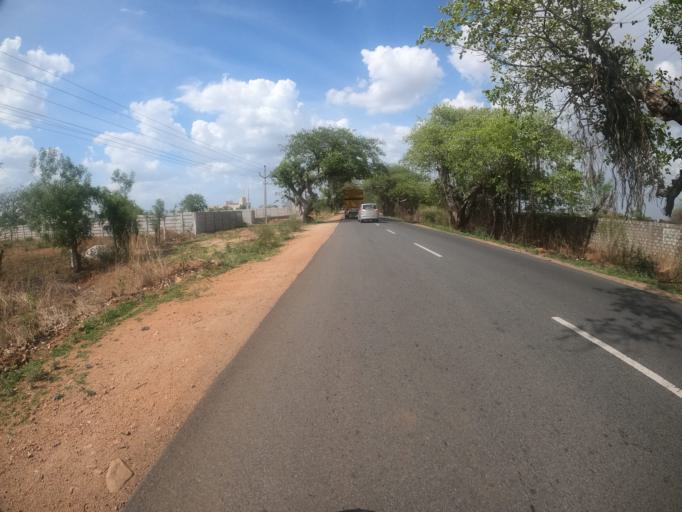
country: IN
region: Telangana
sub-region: Rangareddi
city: Sriramnagar
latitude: 17.3212
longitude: 78.2643
